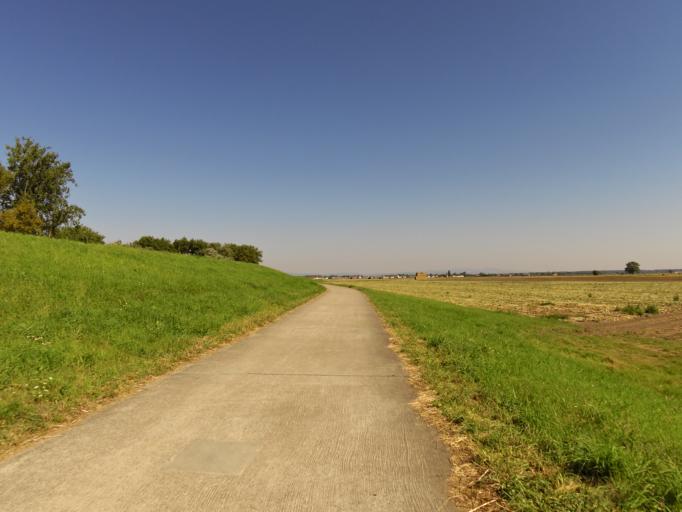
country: DE
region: Rheinland-Pfalz
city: Oppenheim
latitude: 49.8696
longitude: 8.3692
